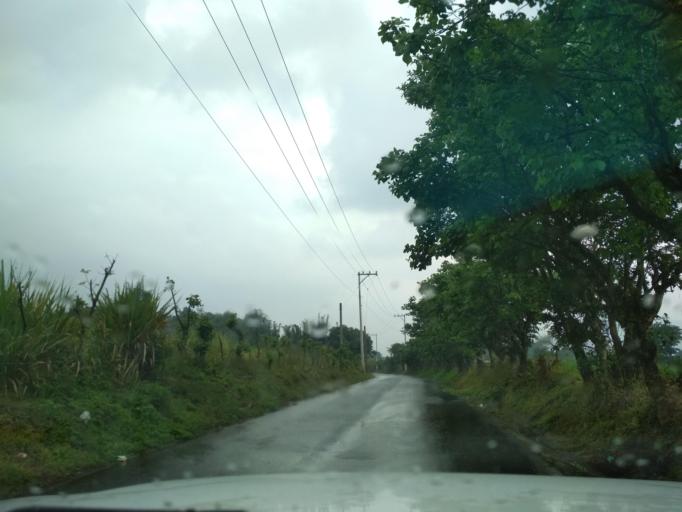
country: MX
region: Veracruz
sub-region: Mariano Escobedo
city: Mariano Escobedo
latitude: 18.9044
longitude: -97.1243
